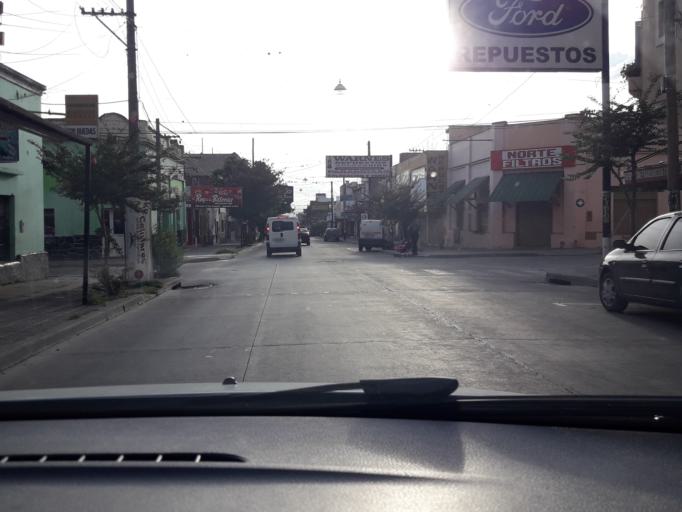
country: AR
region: Jujuy
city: San Salvador de Jujuy
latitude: -24.1915
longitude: -65.2980
